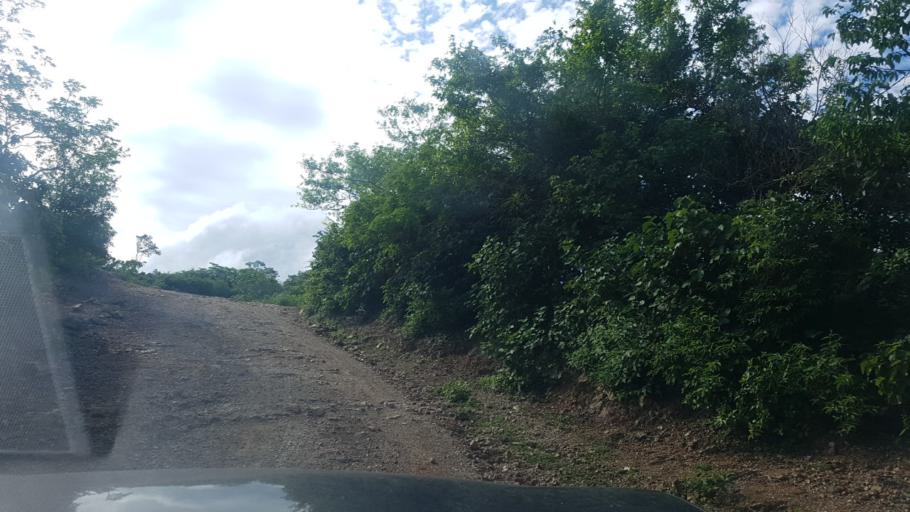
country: NI
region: Nueva Segovia
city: Ocotal
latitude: 13.6063
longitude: -86.4455
